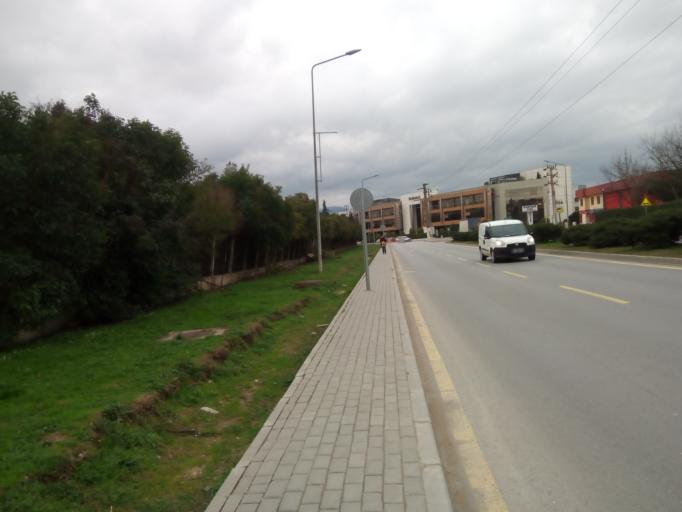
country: TR
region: Bursa
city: Niluefer
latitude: 40.2487
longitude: 28.9557
